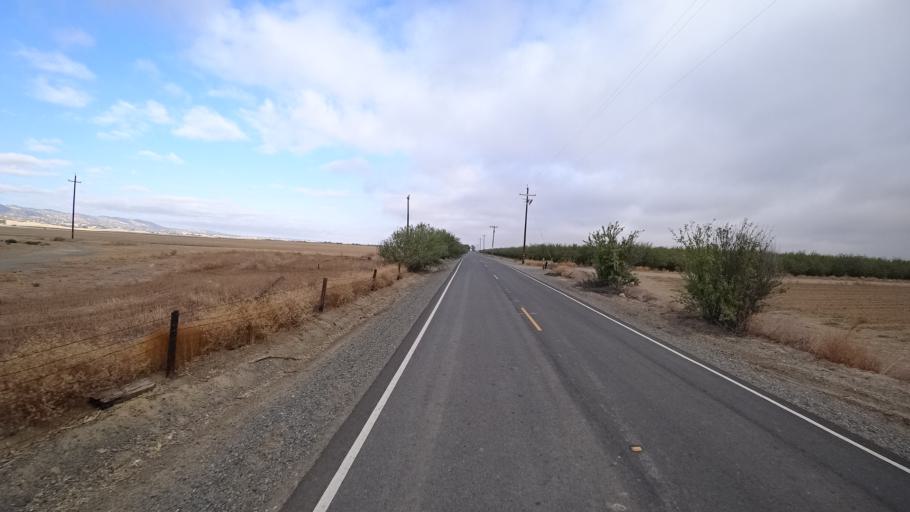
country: US
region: California
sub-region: Yolo County
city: Esparto
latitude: 38.7735
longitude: -122.0440
